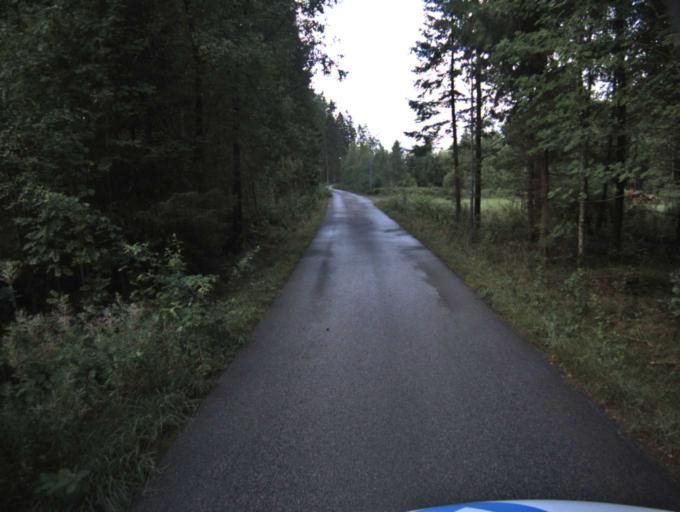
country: SE
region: Vaestra Goetaland
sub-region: Ulricehamns Kommun
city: Ulricehamn
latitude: 57.6738
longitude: 13.4622
